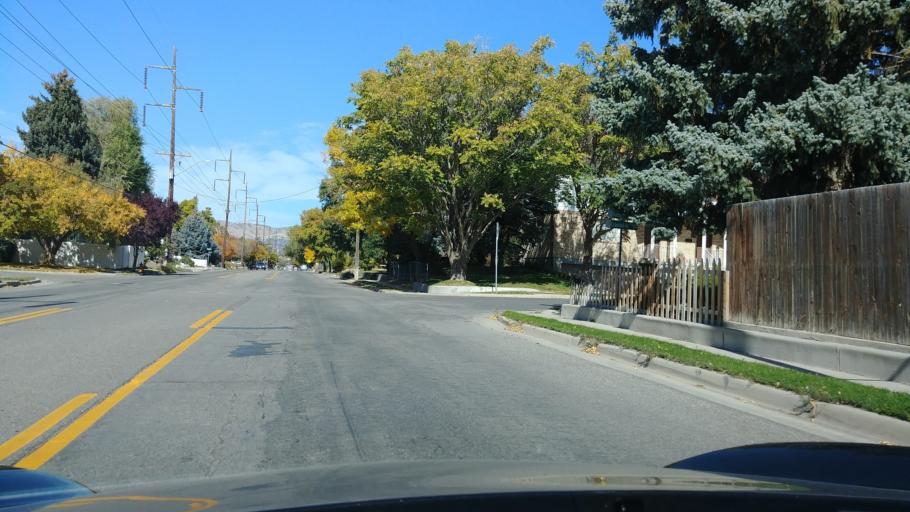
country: US
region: Utah
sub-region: Salt Lake County
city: Millcreek
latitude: 40.7073
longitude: -111.8654
